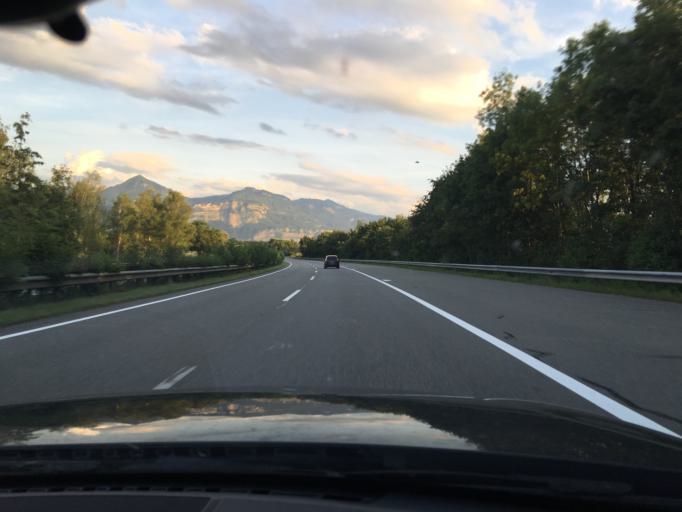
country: AT
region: Vorarlberg
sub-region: Politischer Bezirk Bregenz
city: Lauterach
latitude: 47.4557
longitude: 9.7212
